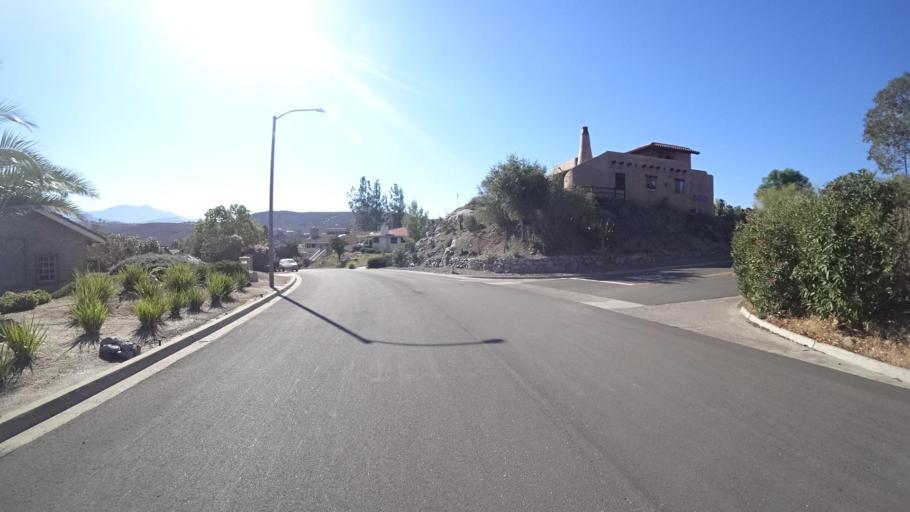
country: US
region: California
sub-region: San Diego County
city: San Diego Country Estates
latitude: 32.9995
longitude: -116.8145
